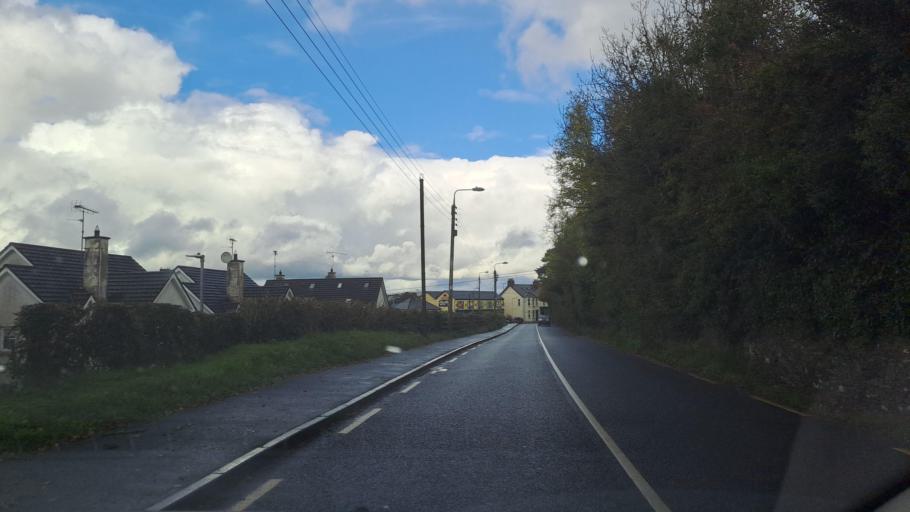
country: IE
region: Ulster
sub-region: An Cabhan
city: Bailieborough
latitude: 53.9131
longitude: -6.9703
